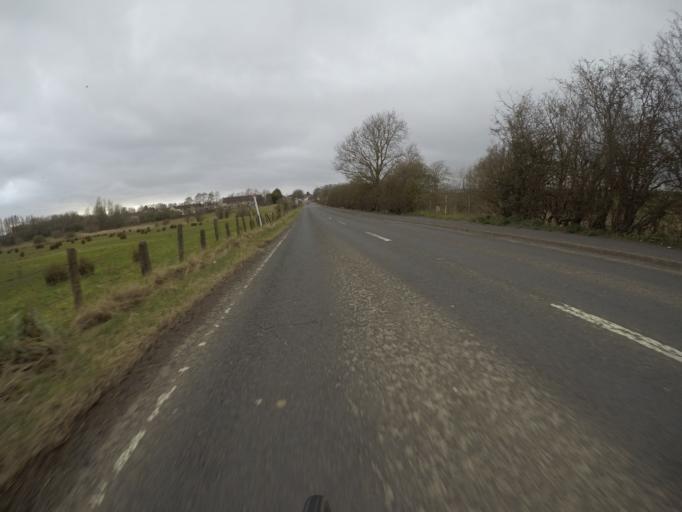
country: GB
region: Scotland
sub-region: North Ayrshire
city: Springside
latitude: 55.6129
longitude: -4.5821
